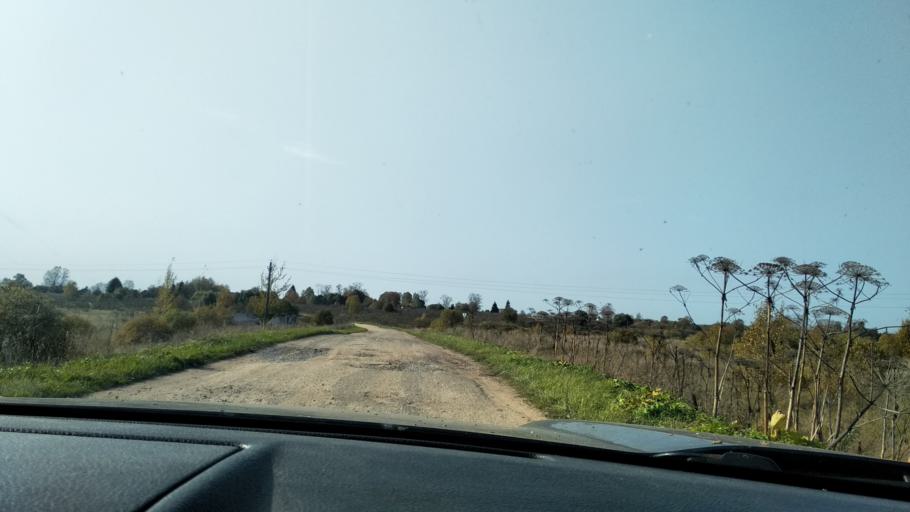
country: RU
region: Tverskaya
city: Krasnyy Kholm
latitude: 58.0322
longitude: 37.1651
